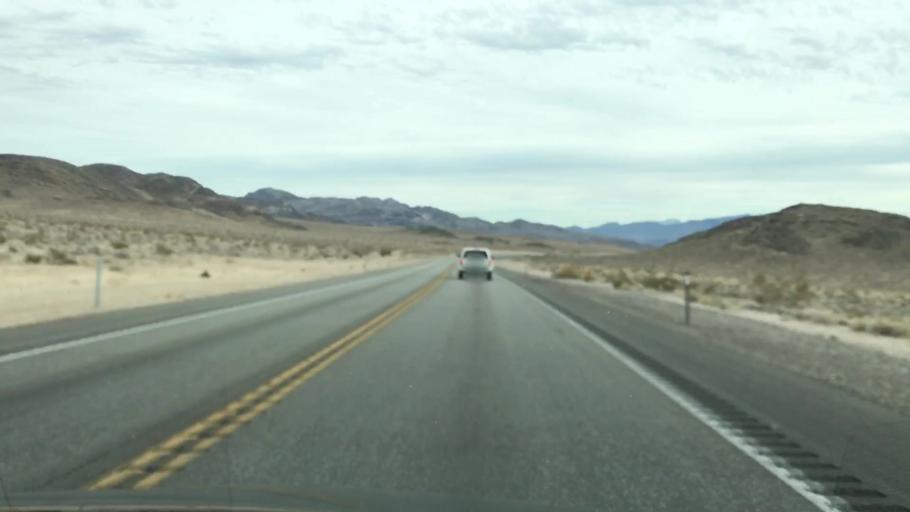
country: US
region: Nevada
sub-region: Nye County
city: Pahrump
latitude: 36.6243
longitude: -116.3044
